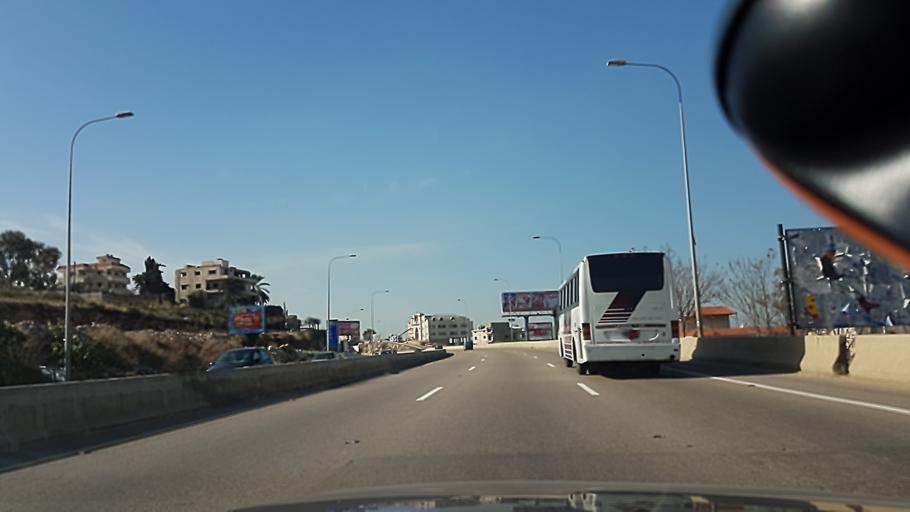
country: LB
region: Liban-Sud
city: Sidon
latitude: 33.6061
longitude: 35.3957
